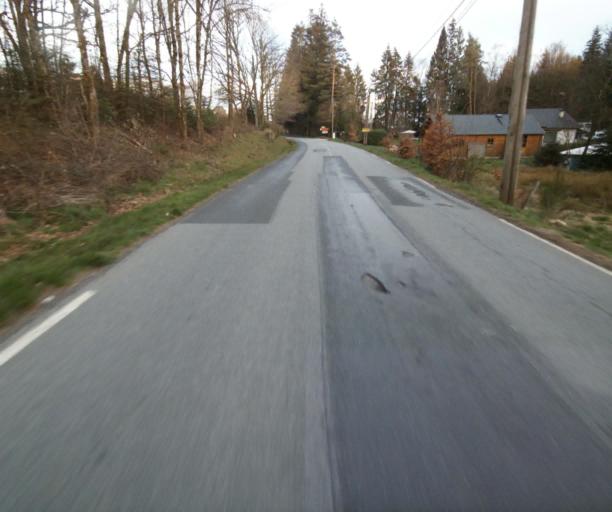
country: FR
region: Limousin
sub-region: Departement de la Correze
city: Correze
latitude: 45.2789
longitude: 1.9648
